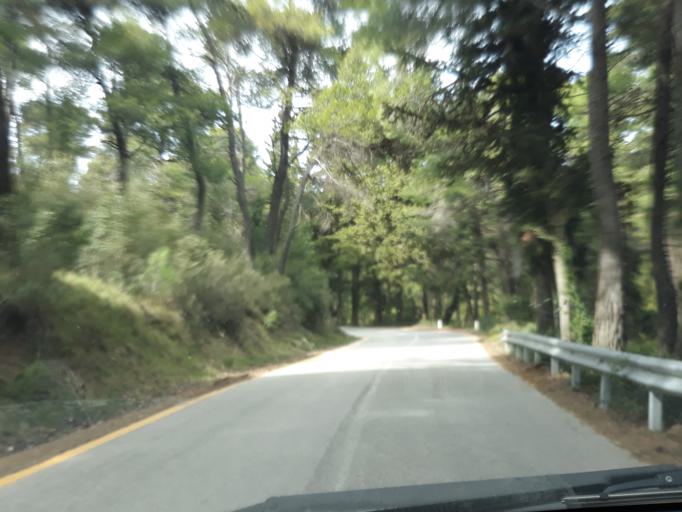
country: GR
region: Attica
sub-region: Nomarchia Anatolikis Attikis
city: Varybobi
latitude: 38.1618
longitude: 23.7884
